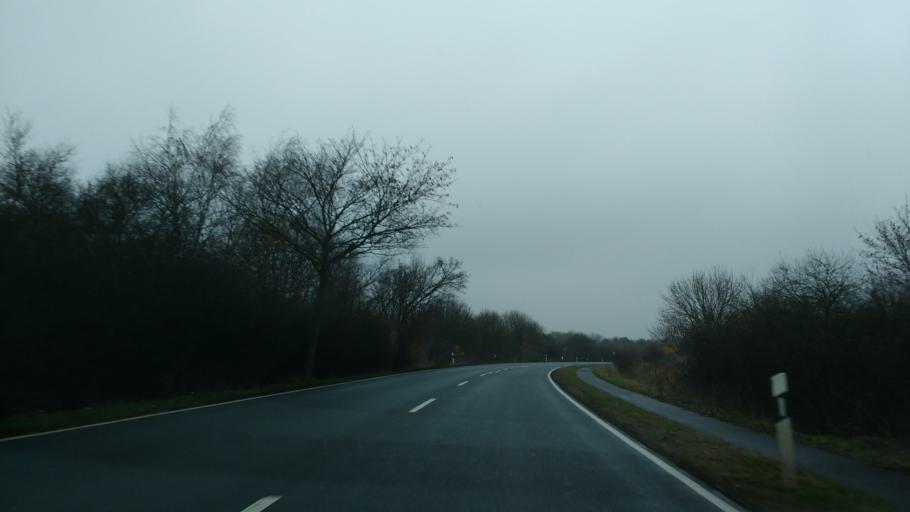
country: DE
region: Lower Saxony
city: Garbsen
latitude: 52.4295
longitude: 9.5724
